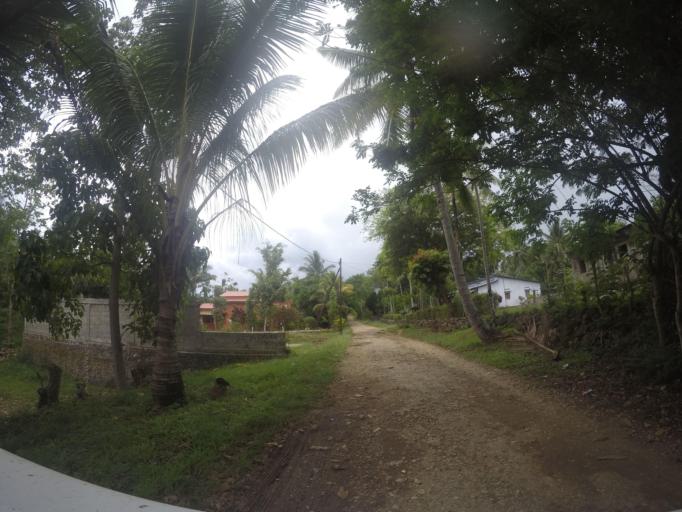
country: TL
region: Lautem
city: Lospalos
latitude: -8.5254
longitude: 126.9941
